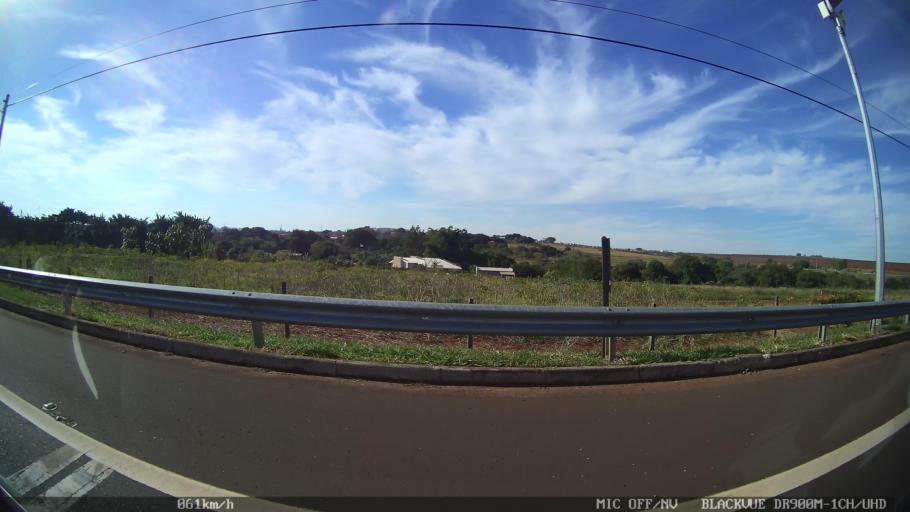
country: BR
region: Sao Paulo
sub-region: Araraquara
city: Araraquara
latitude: -21.7910
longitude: -48.1359
